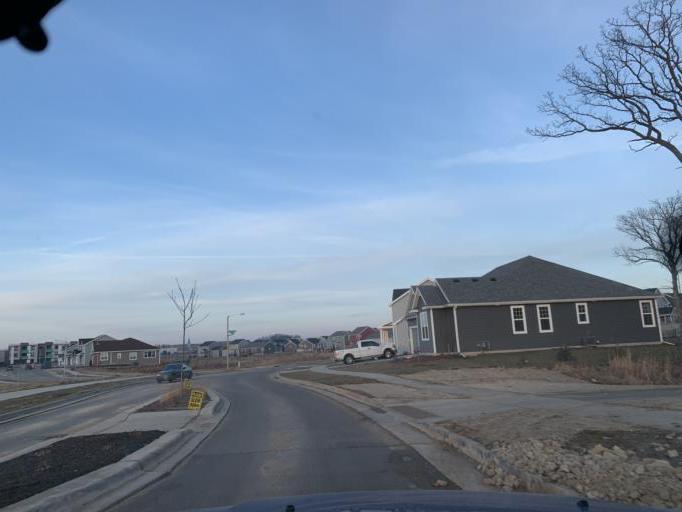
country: US
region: Wisconsin
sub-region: Dane County
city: Verona
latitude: 43.0487
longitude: -89.5596
